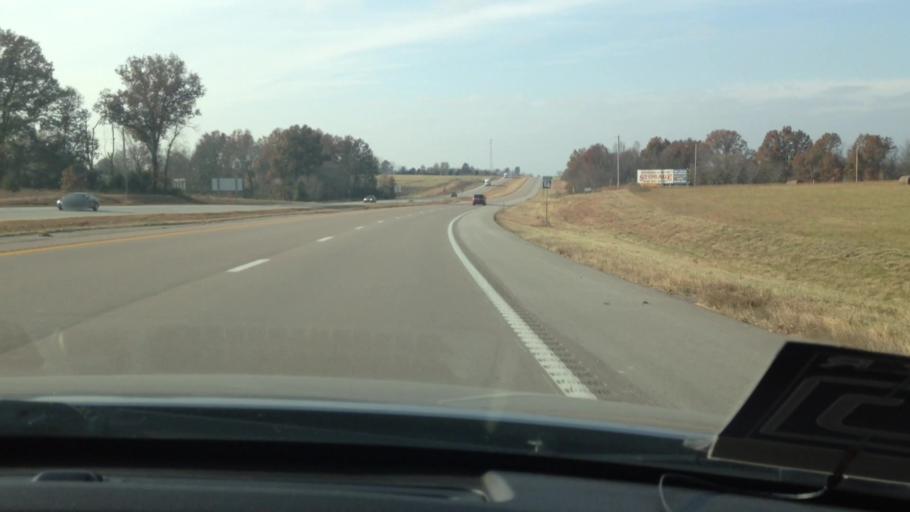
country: US
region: Missouri
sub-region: Cass County
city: Garden City
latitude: 38.4692
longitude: -94.0103
